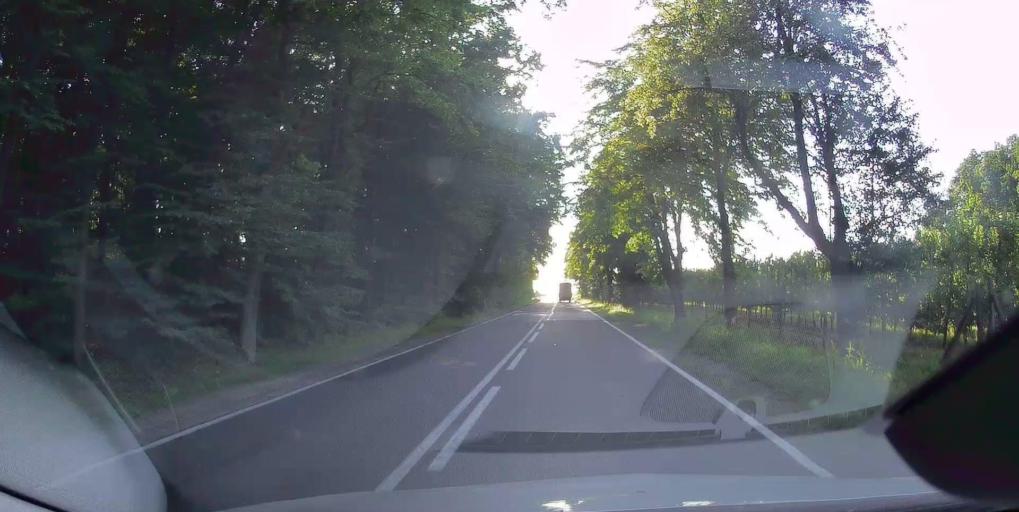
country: PL
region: Lodz Voivodeship
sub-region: Powiat rawski
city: Sadkowice
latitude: 51.8049
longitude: 20.5852
